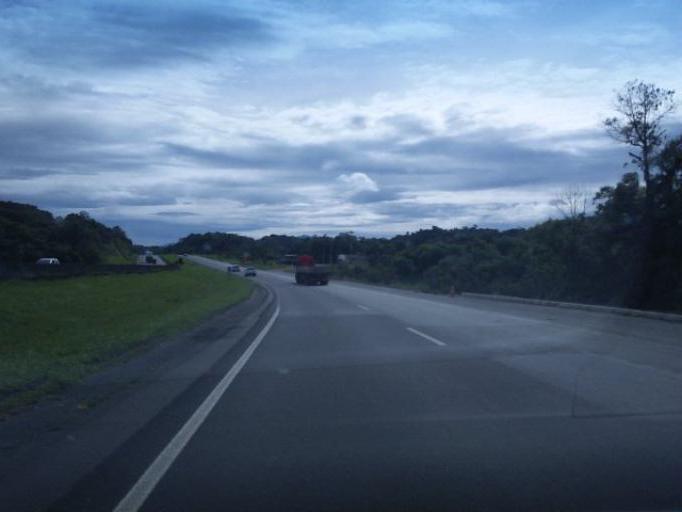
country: BR
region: Sao Paulo
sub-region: Cajati
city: Cajati
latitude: -24.9551
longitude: -48.3319
